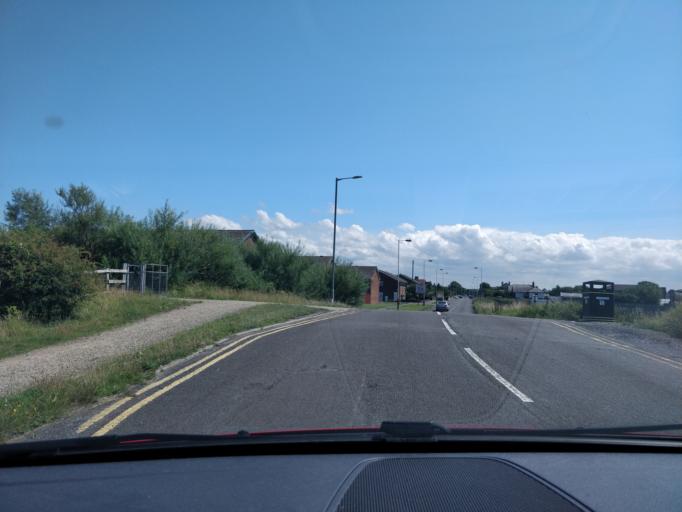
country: GB
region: England
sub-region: Sefton
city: Southport
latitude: 53.6727
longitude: -2.9759
